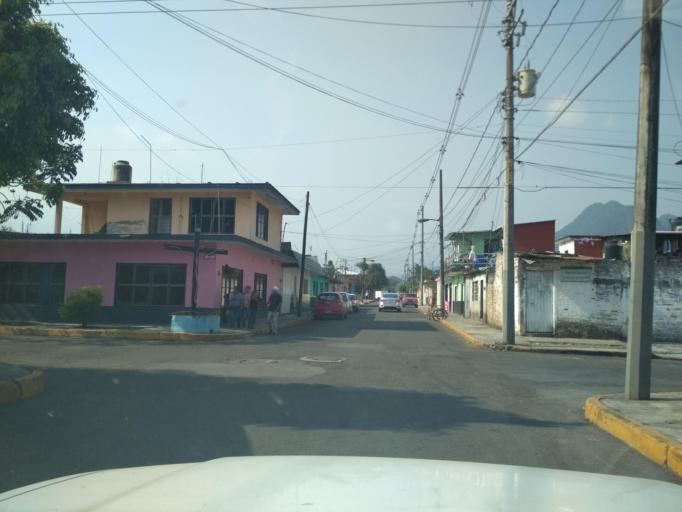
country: MX
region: Veracruz
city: Jalapilla
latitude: 18.8387
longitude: -97.0885
